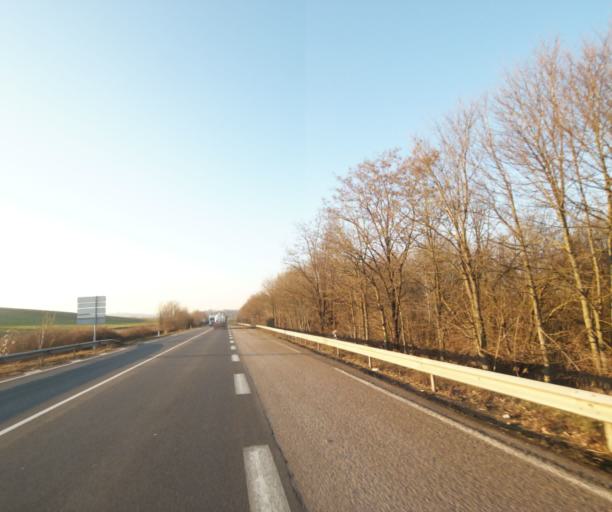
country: FR
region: Champagne-Ardenne
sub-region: Departement de la Haute-Marne
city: Bienville
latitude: 48.5431
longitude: 5.0821
